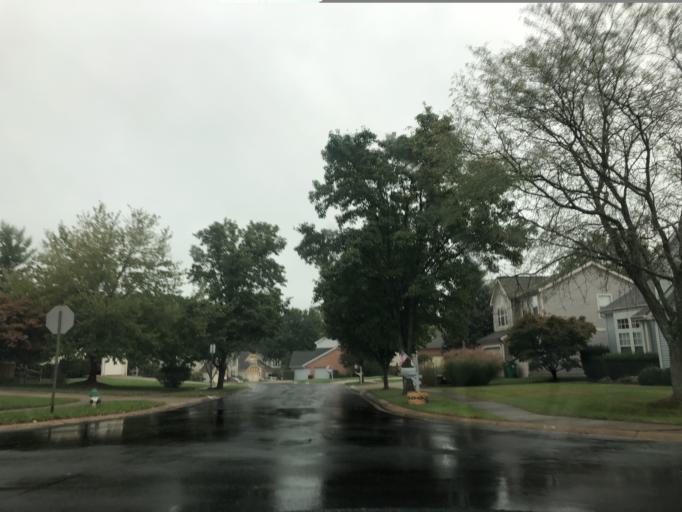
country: US
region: Ohio
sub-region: Hamilton County
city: Loveland
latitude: 39.2669
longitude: -84.2832
